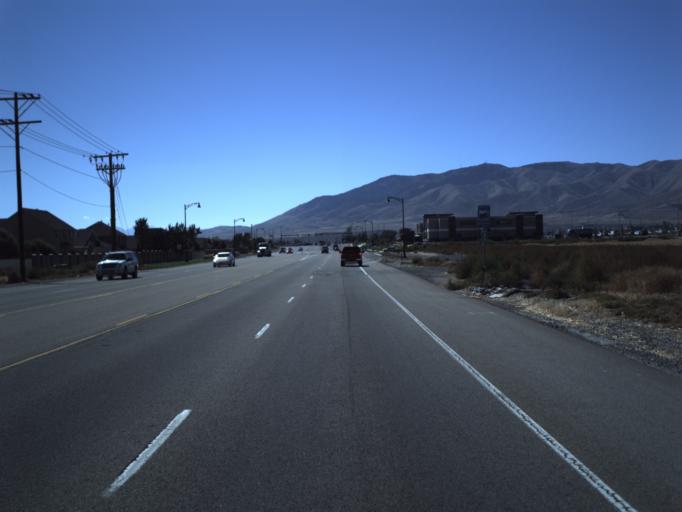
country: US
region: Utah
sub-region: Utah County
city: Saratoga Springs
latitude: 40.3777
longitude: -111.9165
